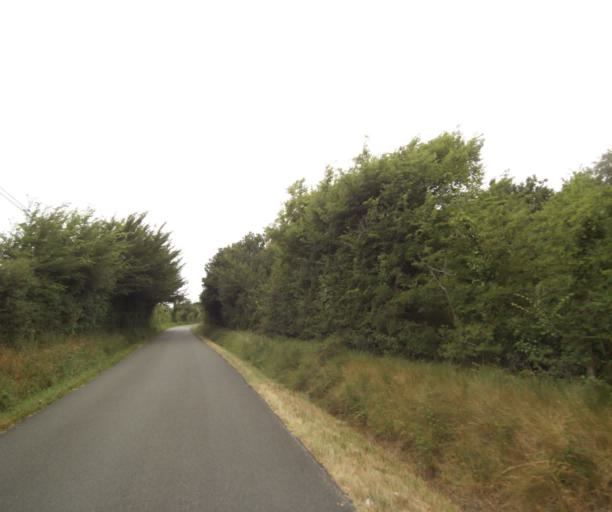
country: FR
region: Pays de la Loire
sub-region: Departement de la Vendee
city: Chateau-d'Olonne
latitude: 46.4651
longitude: -1.7131
